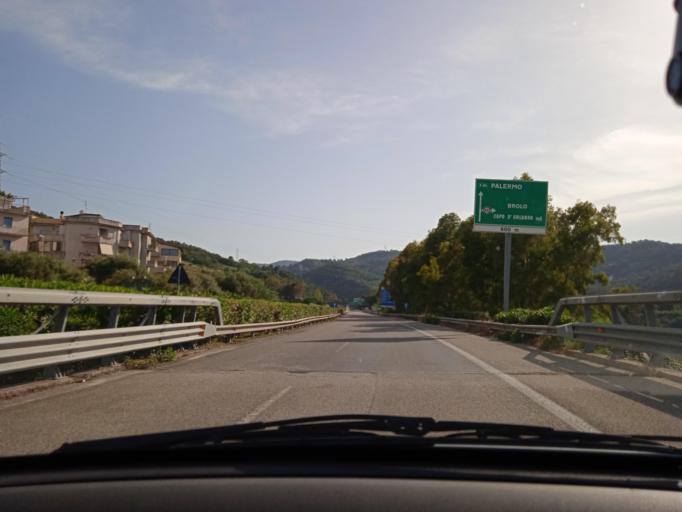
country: IT
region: Sicily
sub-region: Messina
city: Brolo
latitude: 38.1518
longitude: 14.8333
